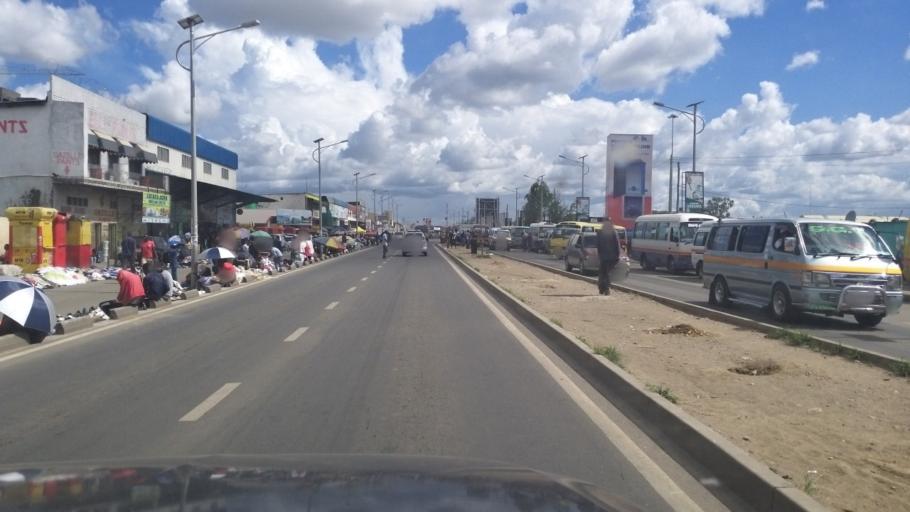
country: ZM
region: Lusaka
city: Lusaka
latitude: -15.4186
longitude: 28.2779
